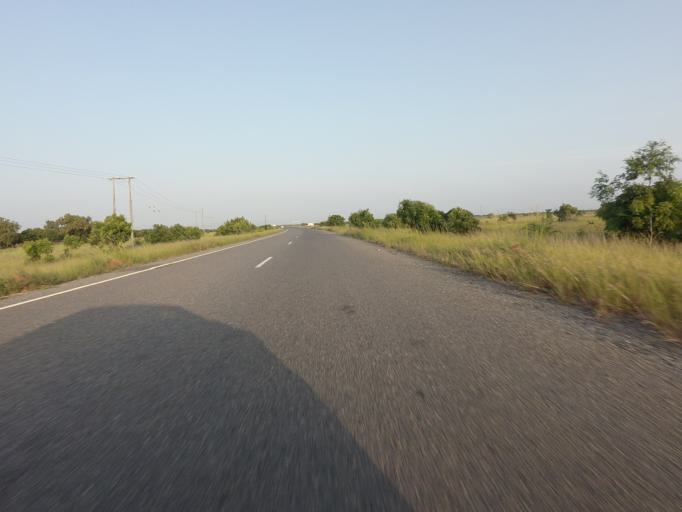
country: GH
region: Volta
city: Anloga
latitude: 5.8802
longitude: 0.7289
